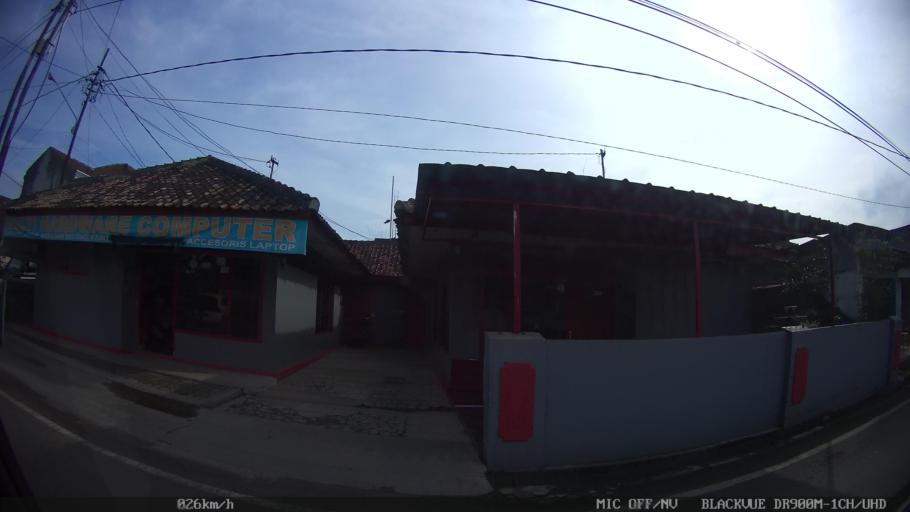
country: ID
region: Lampung
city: Kedaton
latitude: -5.4019
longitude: 105.2633
